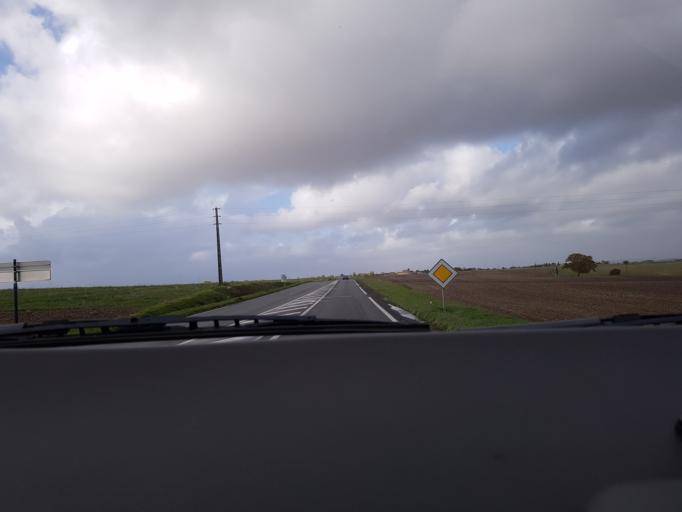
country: FR
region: Poitou-Charentes
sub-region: Departement de la Charente-Maritime
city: Pons
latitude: 45.6419
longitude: -0.5806
